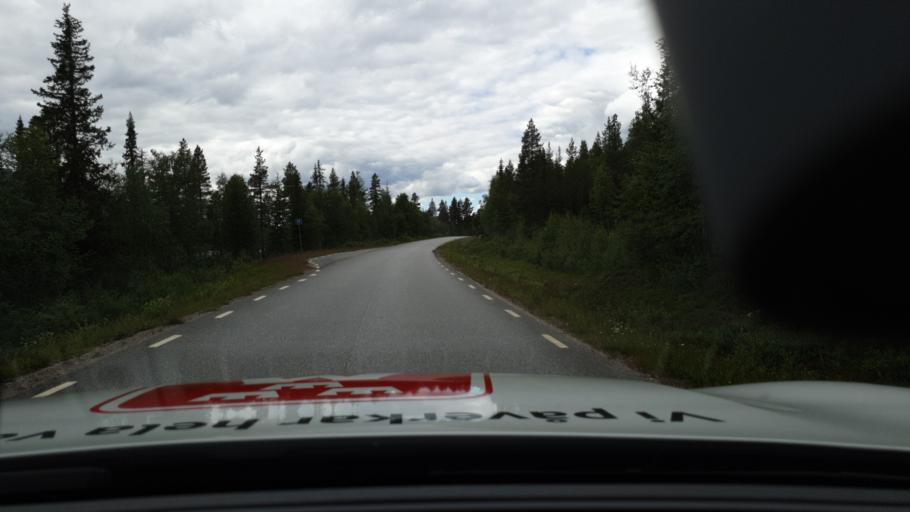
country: SE
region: Norrbotten
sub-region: Arjeplogs Kommun
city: Arjeplog
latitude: 66.8767
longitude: 18.1800
